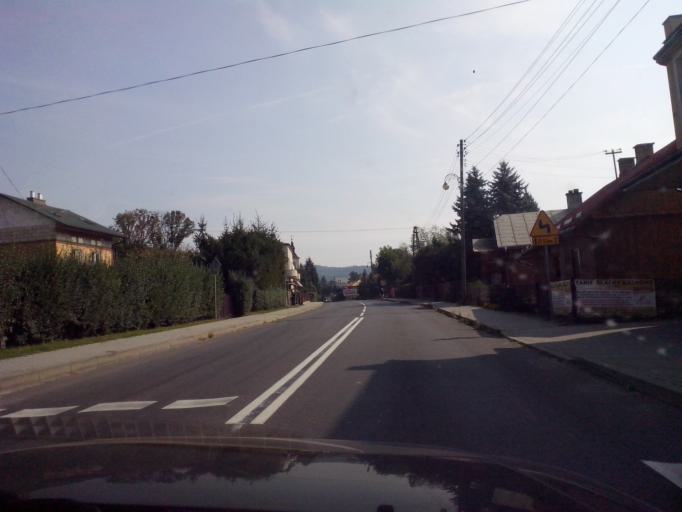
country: PL
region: Subcarpathian Voivodeship
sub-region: Powiat strzyzowski
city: Czudec
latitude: 49.9454
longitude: 21.8311
